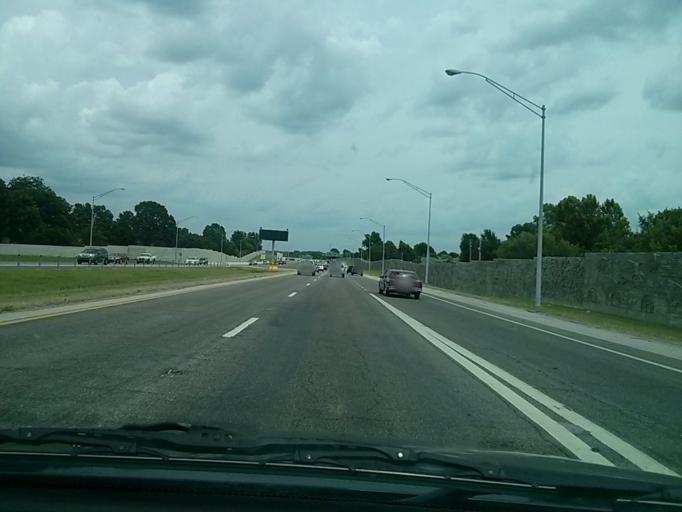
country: US
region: Oklahoma
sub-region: Tulsa County
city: Bixby
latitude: 36.0251
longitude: -95.8797
